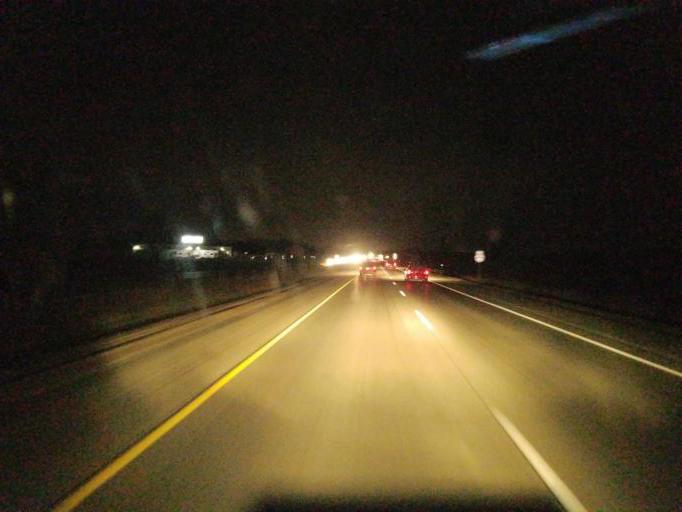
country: US
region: Iowa
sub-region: Dallas County
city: De Soto
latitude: 41.5412
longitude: -94.0028
